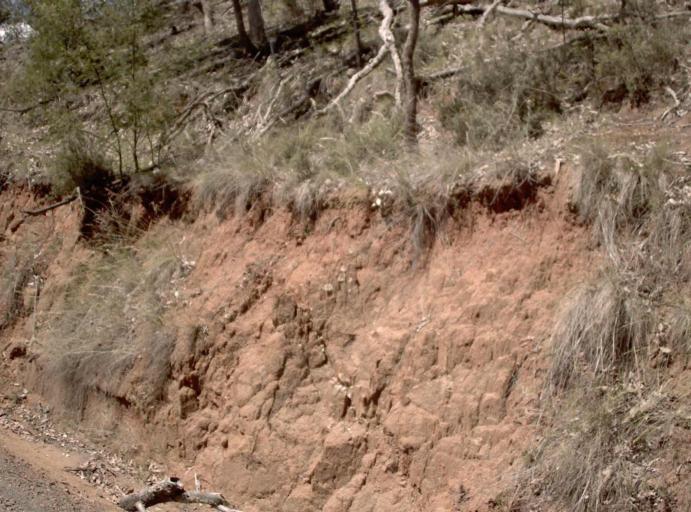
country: AU
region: New South Wales
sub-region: Snowy River
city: Jindabyne
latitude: -37.0559
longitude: 148.5340
